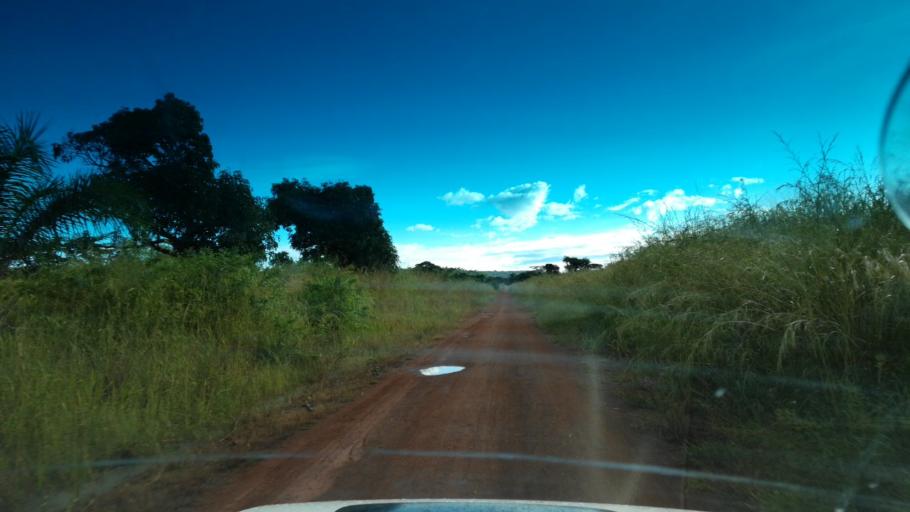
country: ZM
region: Northern
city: Kaputa
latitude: -8.4008
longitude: 28.9405
